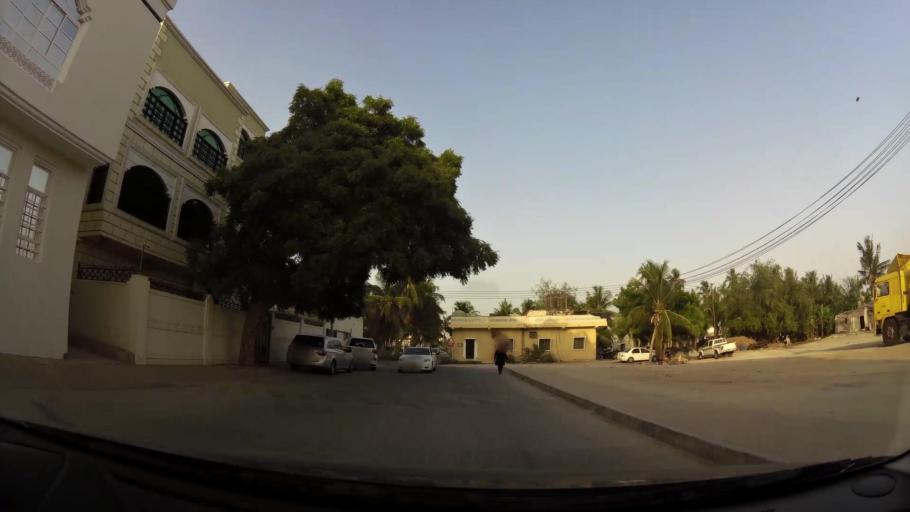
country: OM
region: Zufar
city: Salalah
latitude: 17.0127
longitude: 54.1040
